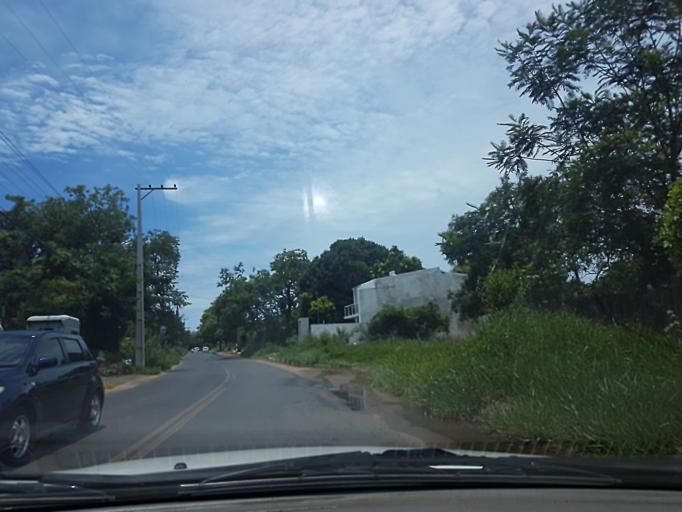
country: PY
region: Central
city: San Lorenzo
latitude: -25.2544
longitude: -57.5049
